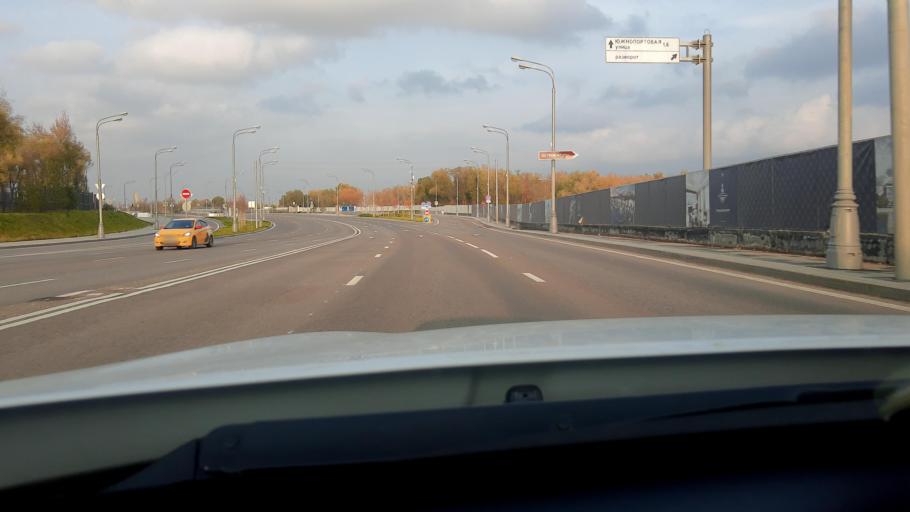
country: RU
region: Moskovskaya
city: Kozhukhovo
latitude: 55.6906
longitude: 37.6772
